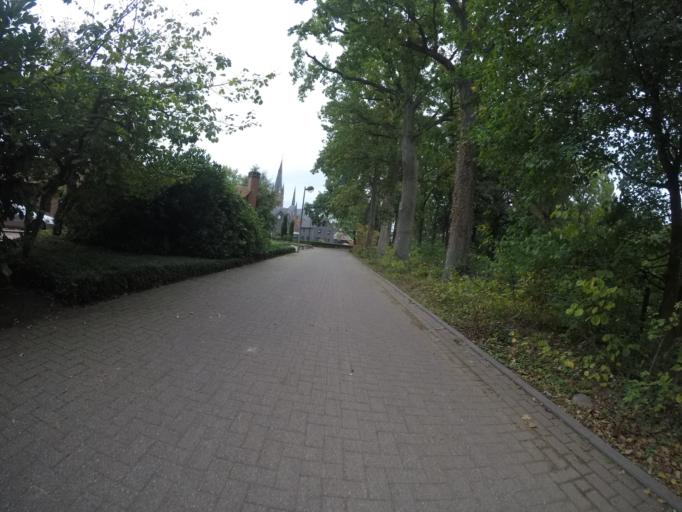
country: DE
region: North Rhine-Westphalia
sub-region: Regierungsbezirk Munster
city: Rhede
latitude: 51.8417
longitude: 6.6939
